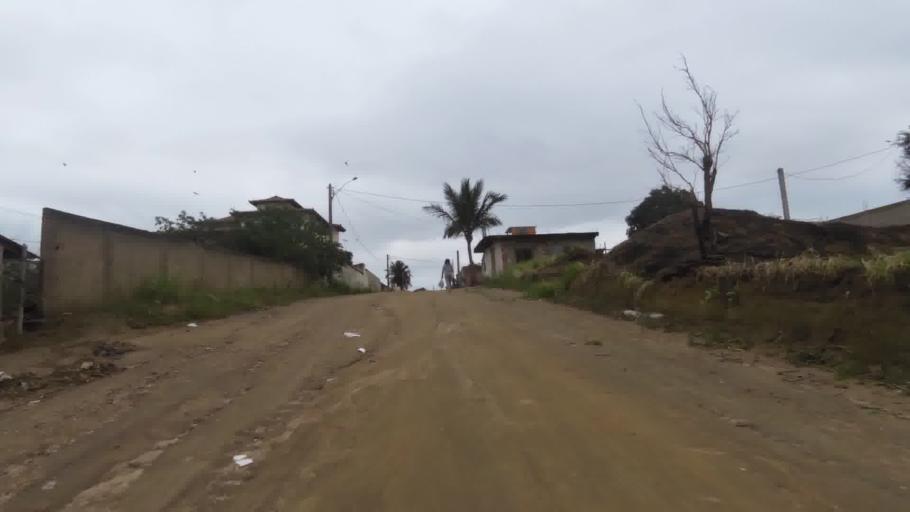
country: BR
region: Espirito Santo
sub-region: Marataizes
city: Marataizes
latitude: -21.0448
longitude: -40.8384
